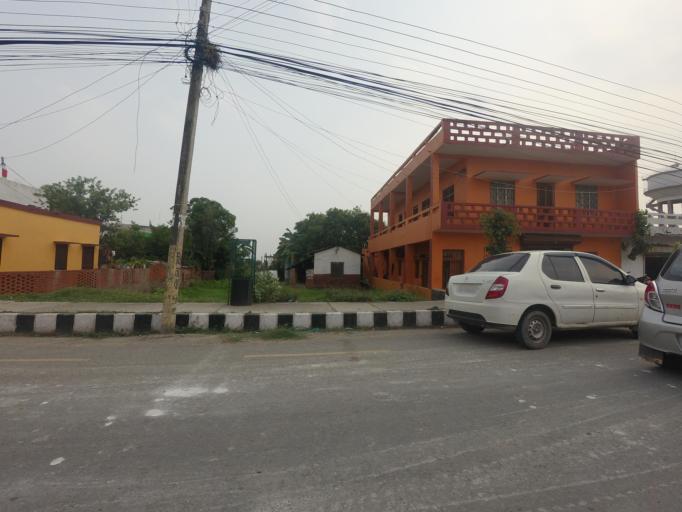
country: NP
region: Western Region
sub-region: Lumbini Zone
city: Bhairahawa
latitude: 27.5084
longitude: 83.4232
